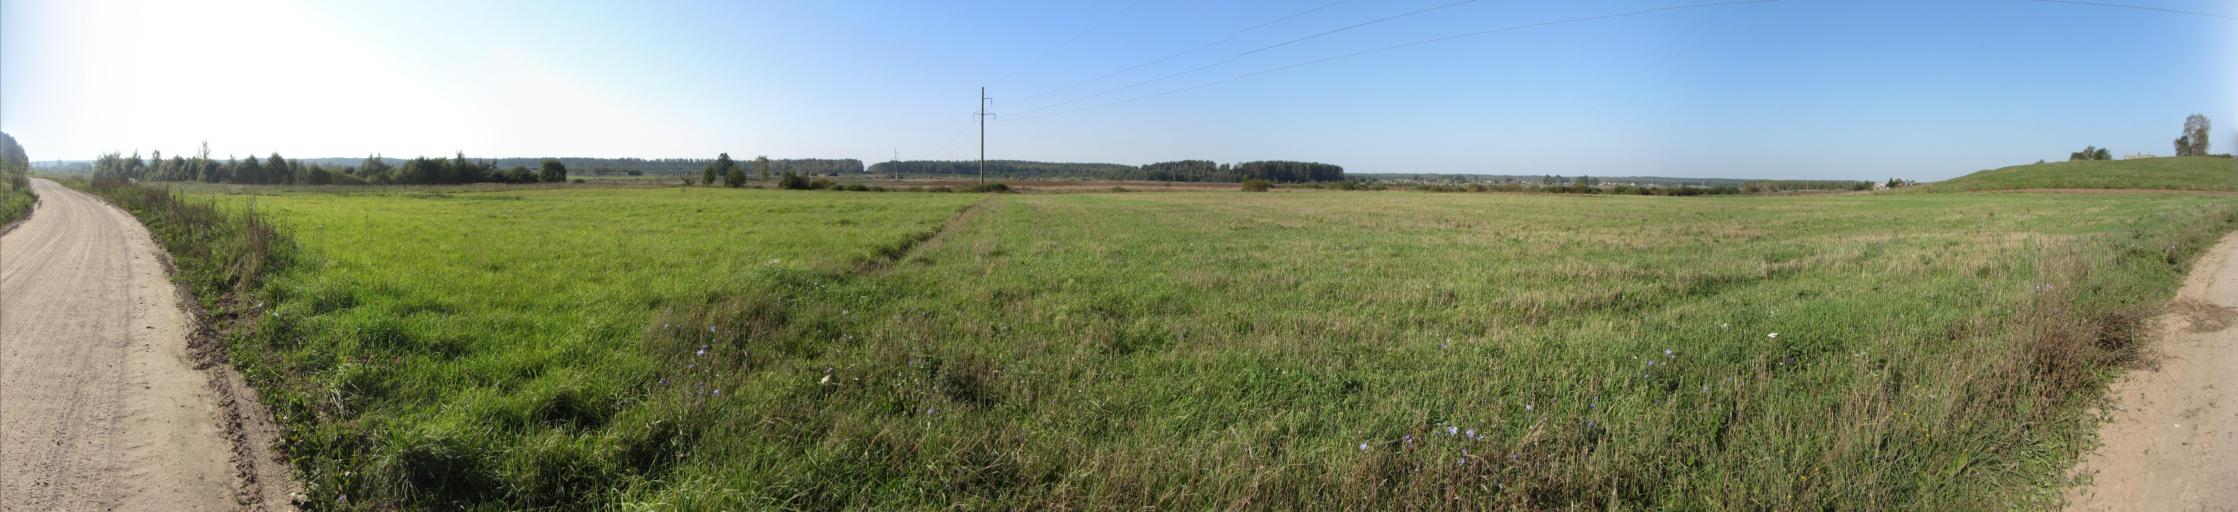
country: LT
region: Vilnius County
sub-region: Trakai
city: Rudiskes
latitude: 54.5731
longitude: 24.8733
